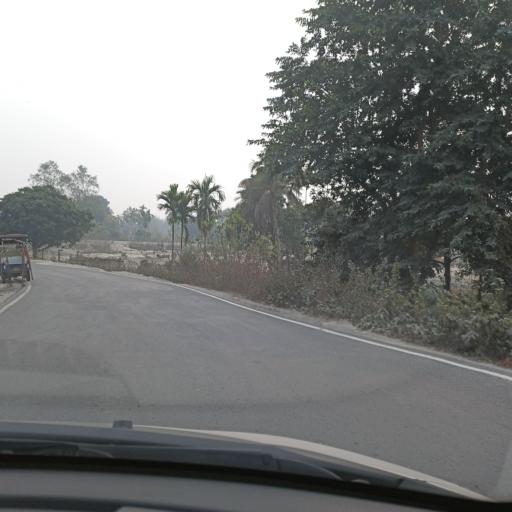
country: IN
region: West Bengal
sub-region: Jalpaiguri
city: Odlabari
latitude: 26.7461
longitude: 88.5800
